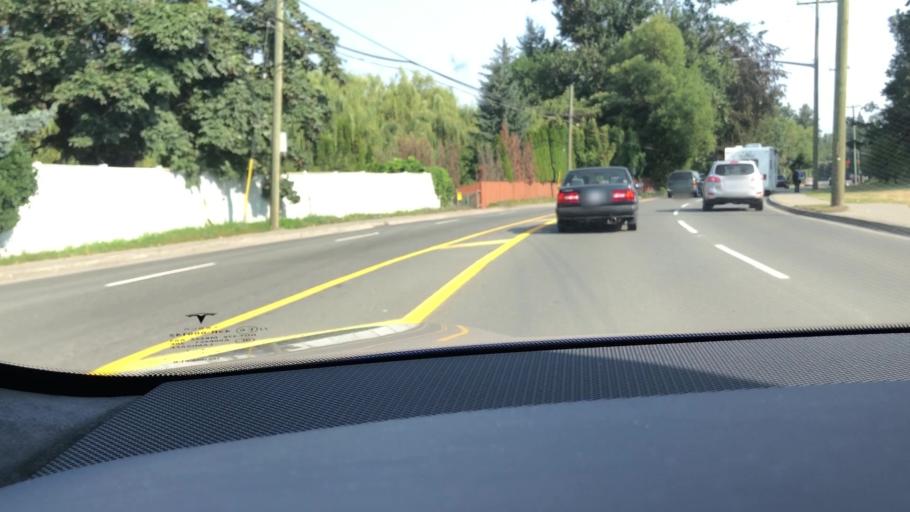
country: CA
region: British Columbia
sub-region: Fraser Valley Regional District
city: Chilliwack
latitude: 49.1248
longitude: -121.9604
